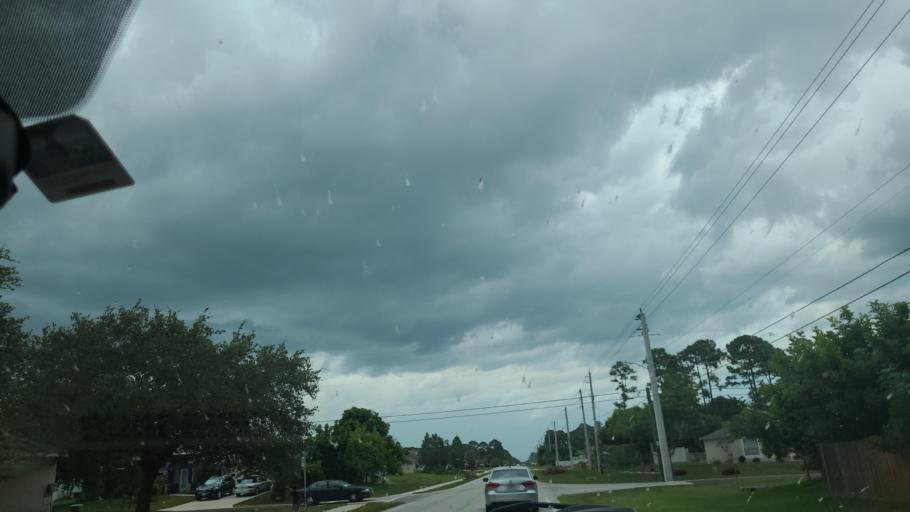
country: US
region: Florida
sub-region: Saint Lucie County
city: Port Saint Lucie
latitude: 27.2392
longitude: -80.3997
